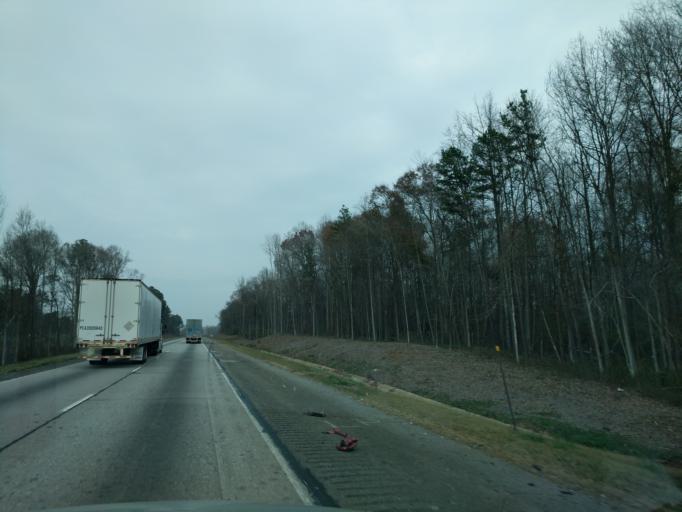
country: US
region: Georgia
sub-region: Jackson County
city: Commerce
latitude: 34.2746
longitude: -83.4353
